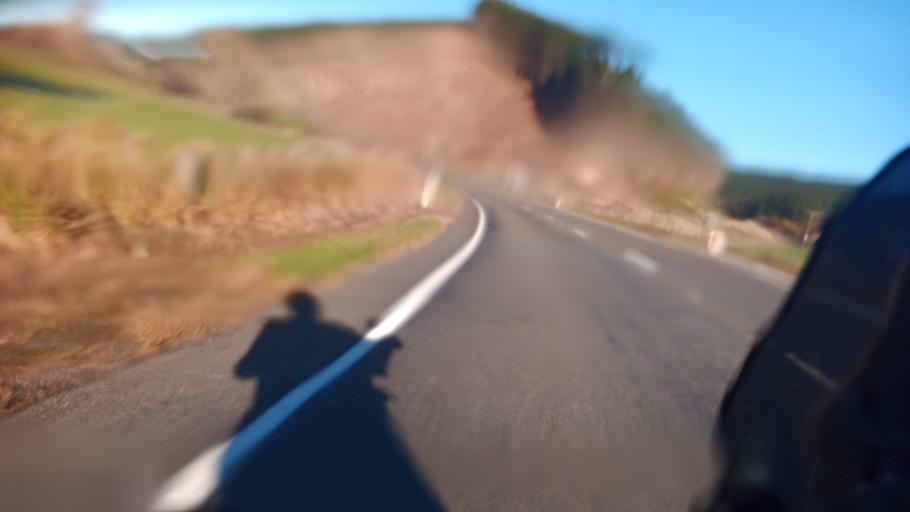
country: NZ
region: Hawke's Bay
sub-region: Wairoa District
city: Wairoa
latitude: -39.0210
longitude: 177.3199
